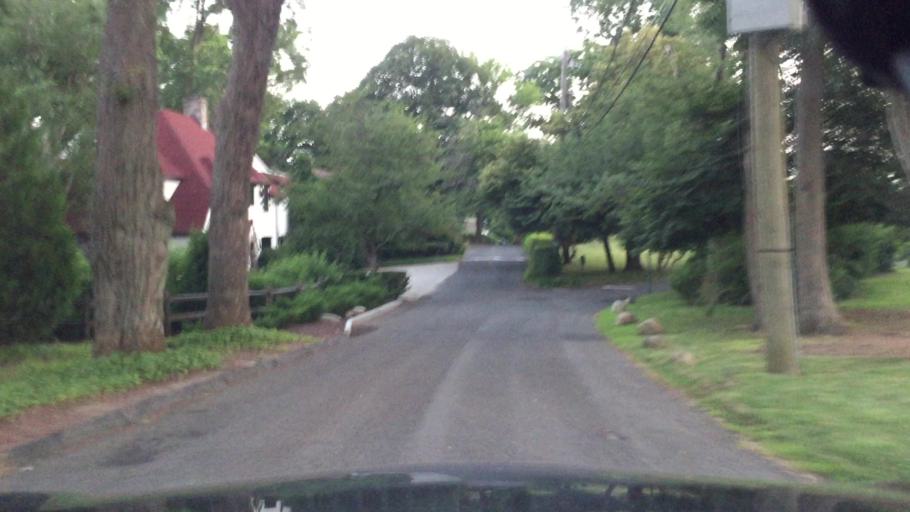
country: US
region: Connecticut
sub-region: Fairfield County
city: Darien
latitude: 41.0657
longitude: -73.4271
